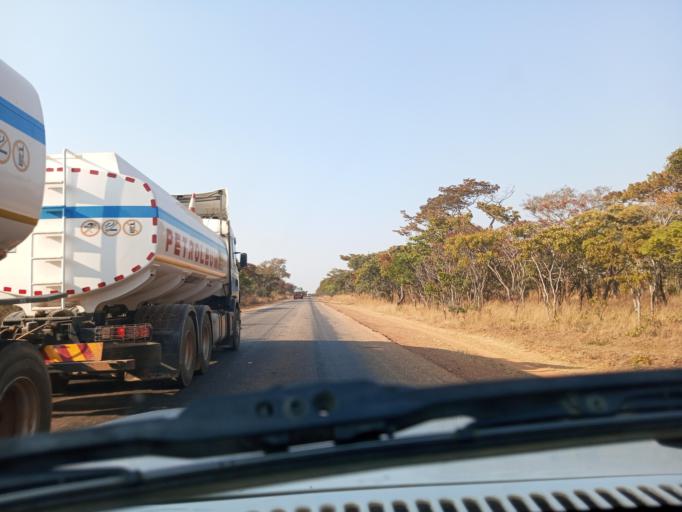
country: ZM
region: Northern
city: Mpika
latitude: -12.3611
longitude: 31.1043
